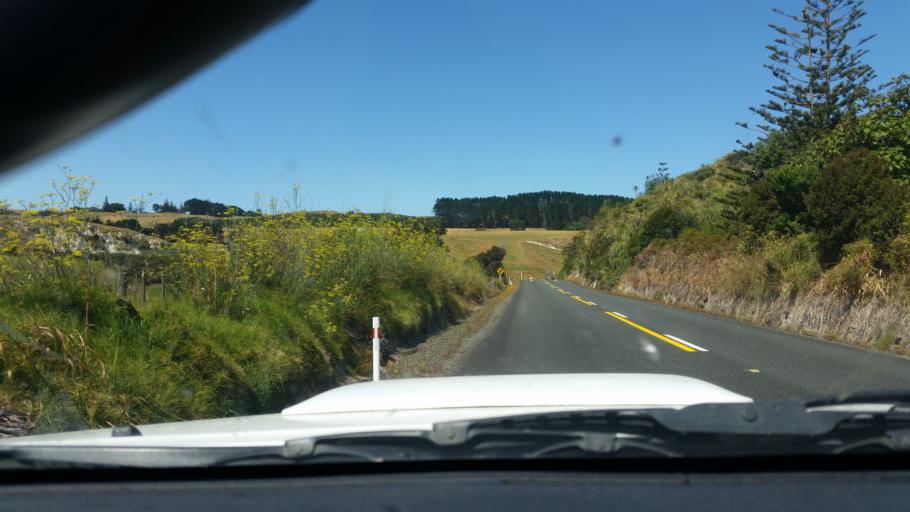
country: NZ
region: Northland
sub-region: Kaipara District
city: Dargaville
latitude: -35.8328
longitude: 173.6628
